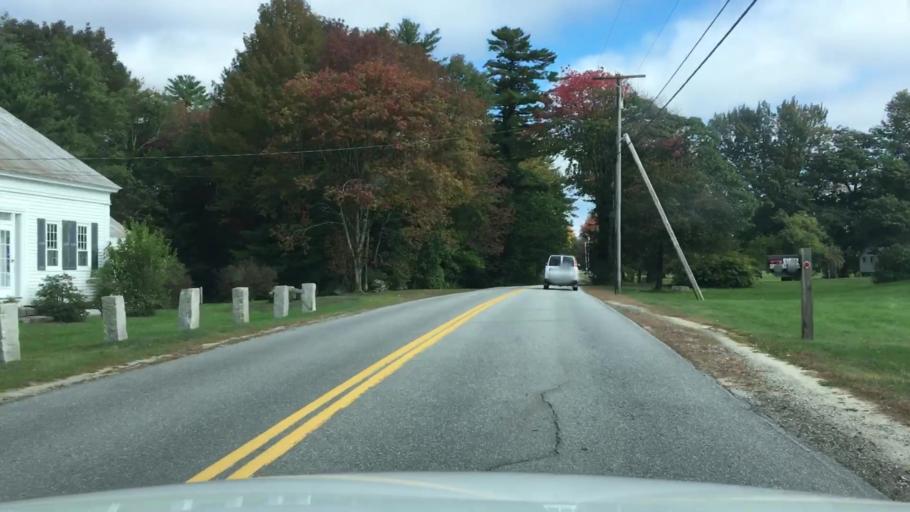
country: US
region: Maine
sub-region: Cumberland County
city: Brunswick
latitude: 43.9261
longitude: -69.9157
